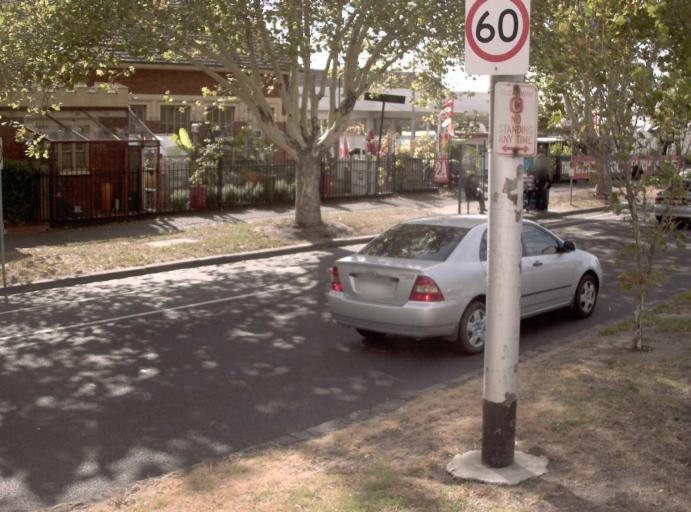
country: AU
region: Victoria
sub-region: Port Phillip
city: Saint Kilda
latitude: -37.8711
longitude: 144.9891
